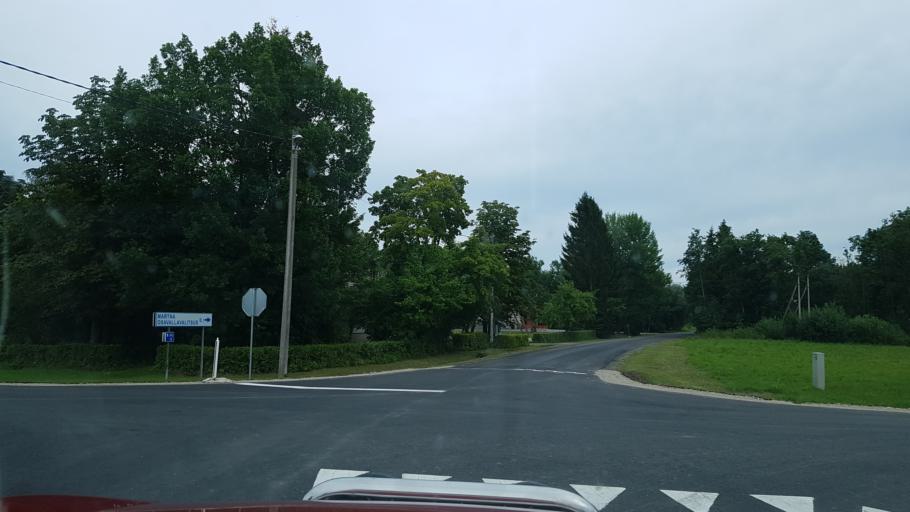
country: EE
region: Laeaene
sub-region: Lihula vald
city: Lihula
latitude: 58.8550
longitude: 23.8009
